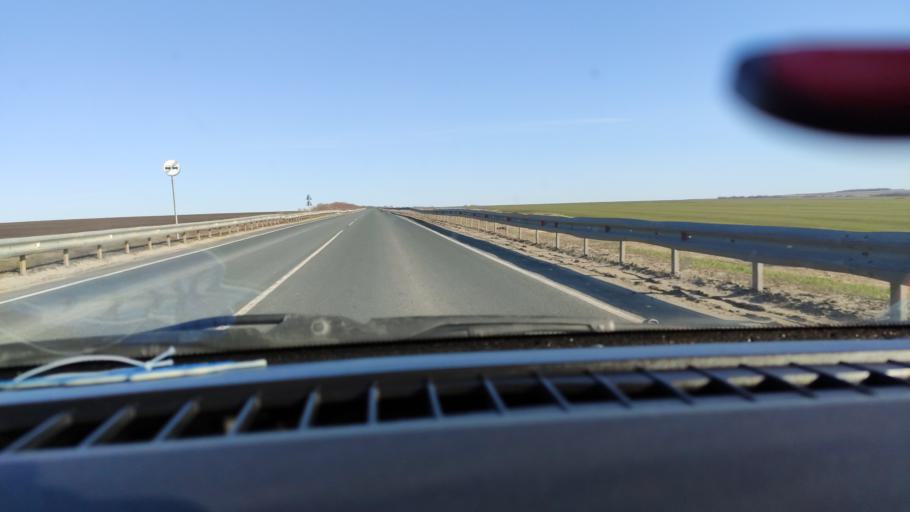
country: RU
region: Saratov
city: Dukhovnitskoye
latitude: 52.7533
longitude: 48.2466
